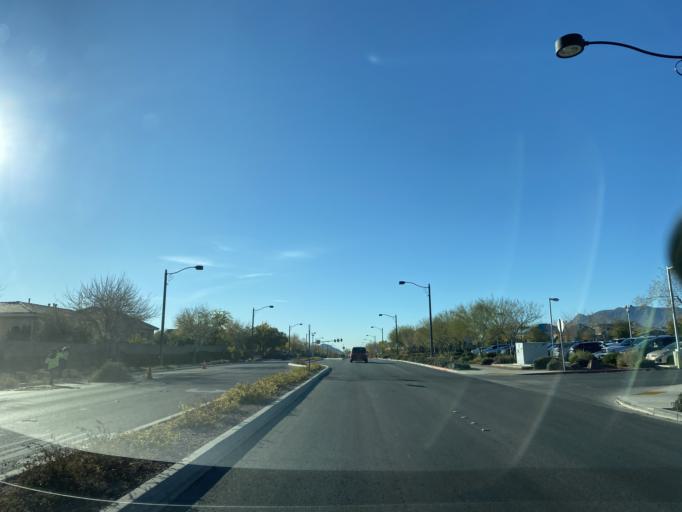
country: US
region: Nevada
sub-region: Clark County
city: Summerlin South
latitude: 36.2971
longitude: -115.3196
